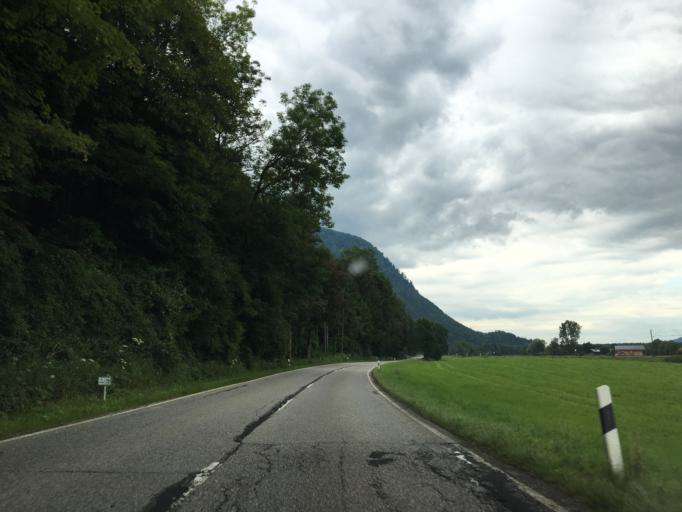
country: AT
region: Tyrol
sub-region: Politischer Bezirk Kufstein
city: Erl
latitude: 47.6713
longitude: 12.1655
